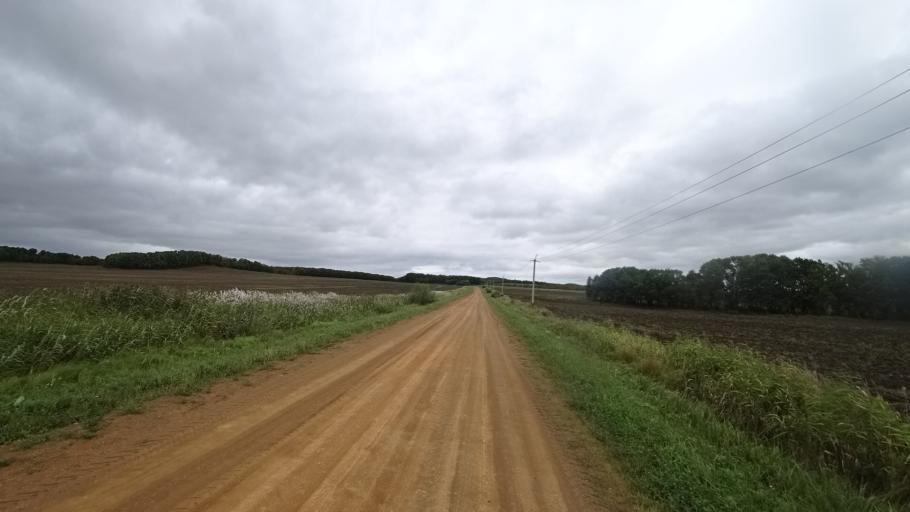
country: RU
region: Primorskiy
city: Chernigovka
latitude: 44.4460
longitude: 132.5962
